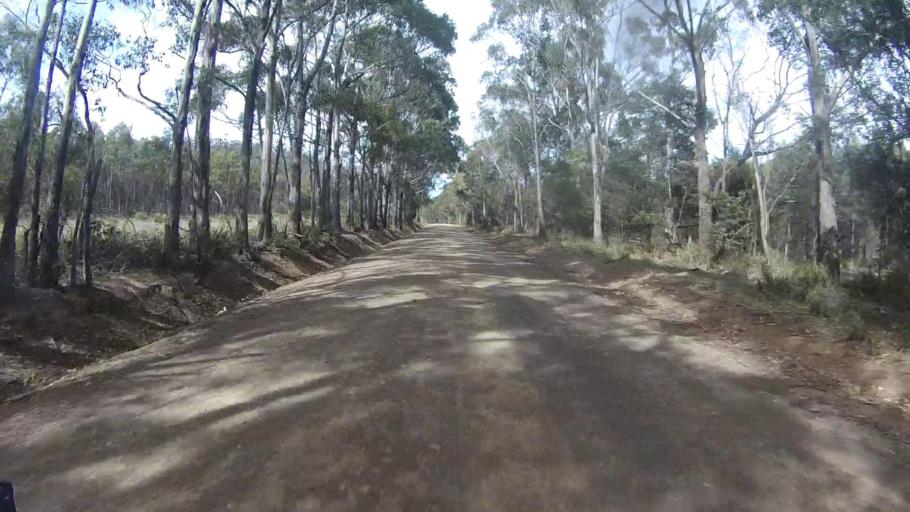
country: AU
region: Tasmania
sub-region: Sorell
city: Sorell
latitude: -42.6637
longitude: 147.8908
